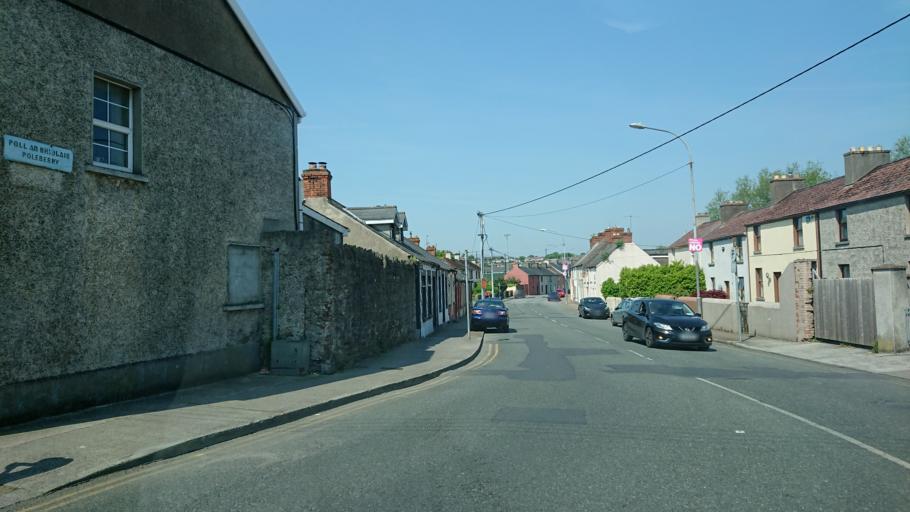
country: IE
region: Munster
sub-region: Waterford
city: Waterford
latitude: 52.2511
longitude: -7.1099
